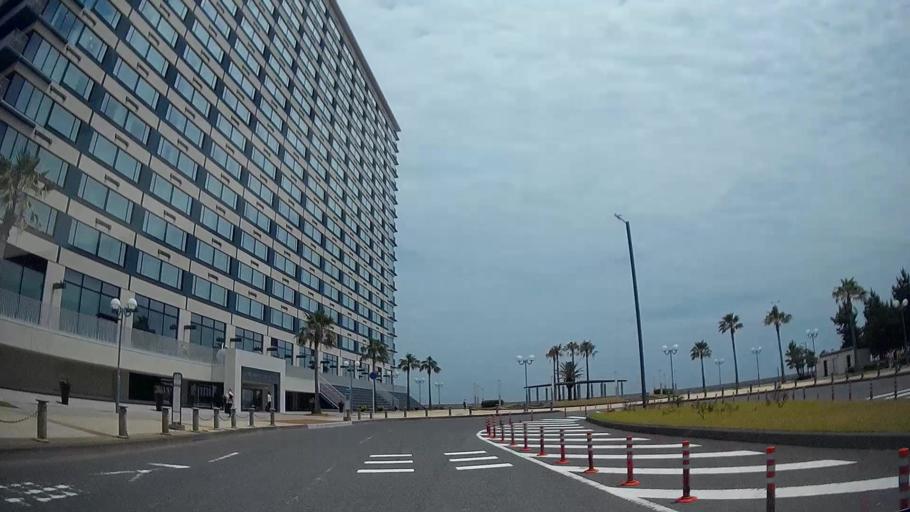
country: JP
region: Tokyo
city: Urayasu
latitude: 35.6376
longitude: 139.9312
